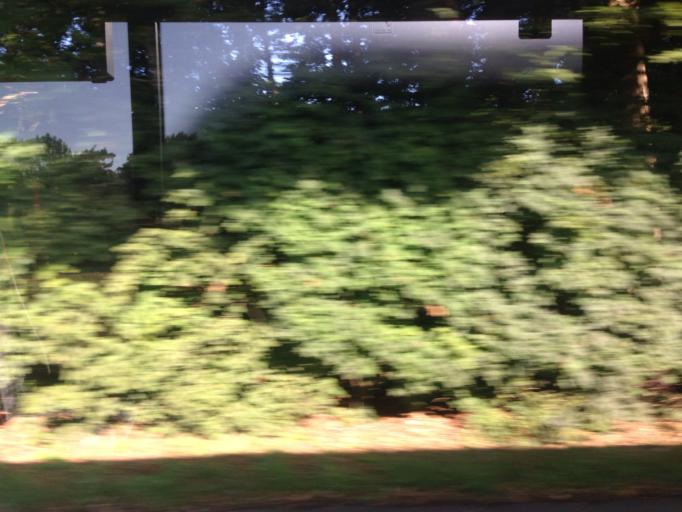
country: DE
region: North Rhine-Westphalia
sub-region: Regierungsbezirk Munster
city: Senden
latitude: 51.8767
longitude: 7.4949
